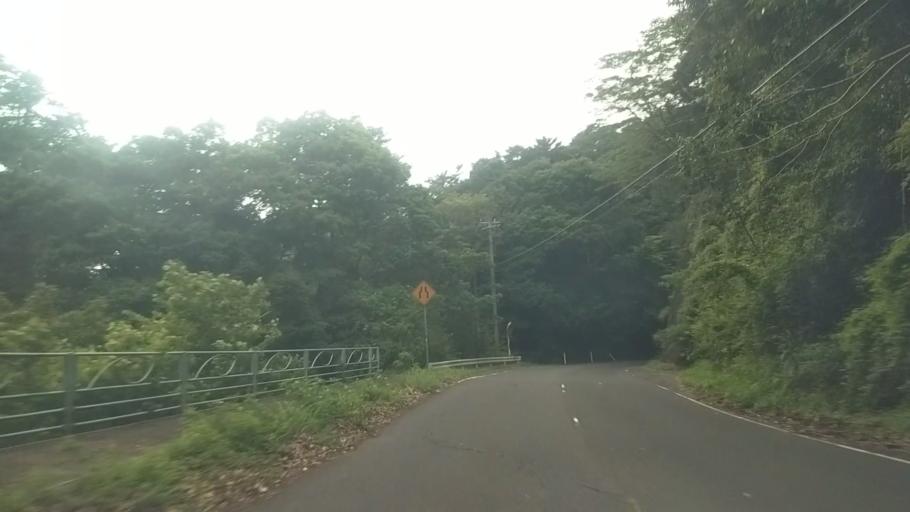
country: JP
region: Chiba
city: Kawaguchi
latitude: 35.1639
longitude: 140.1407
